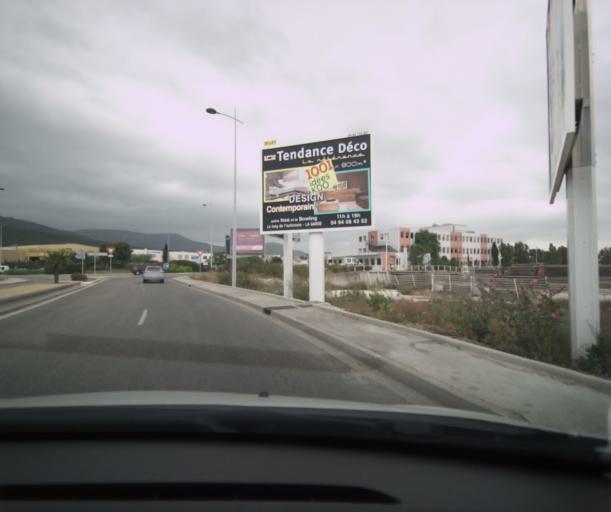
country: FR
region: Provence-Alpes-Cote d'Azur
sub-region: Departement du Var
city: La Garde
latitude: 43.1378
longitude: 6.0338
